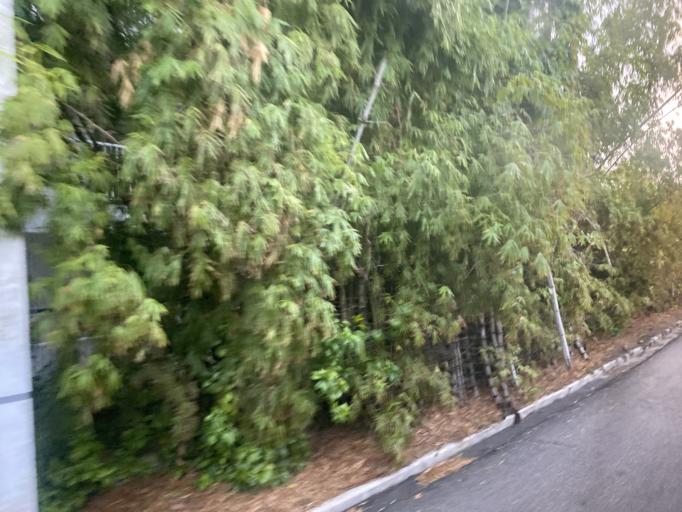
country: DO
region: San Juan
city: Punta Cana
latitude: 18.7209
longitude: -68.4586
